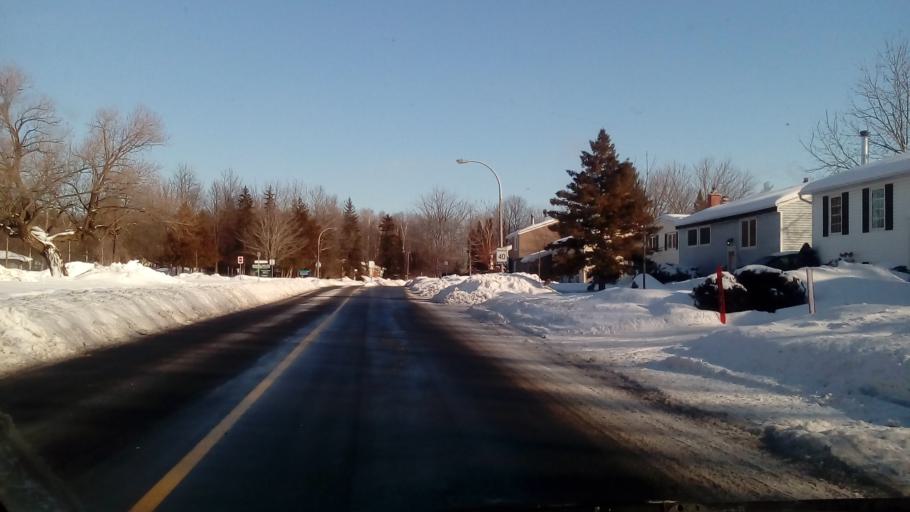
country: CA
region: Ontario
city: Ottawa
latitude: 45.4359
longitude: -75.6229
